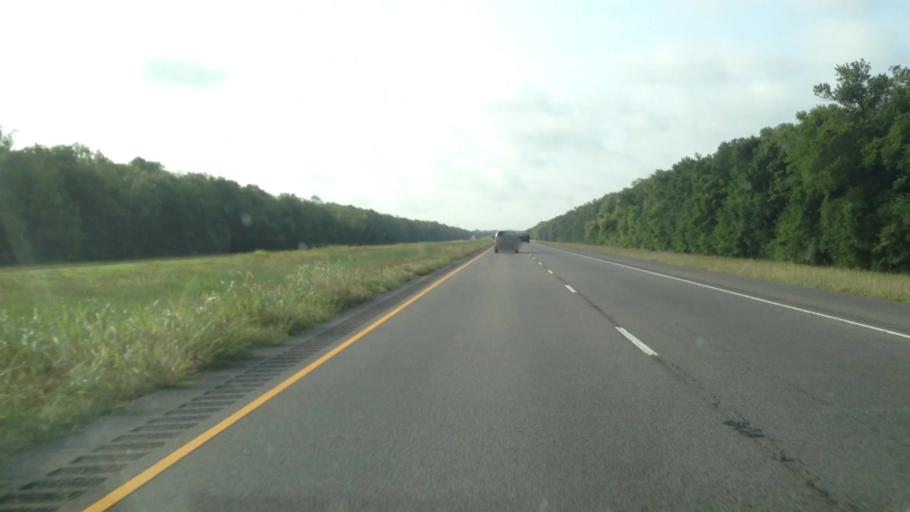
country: US
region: Louisiana
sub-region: Avoyelles Parish
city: Bunkie
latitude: 30.9122
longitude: -92.2411
